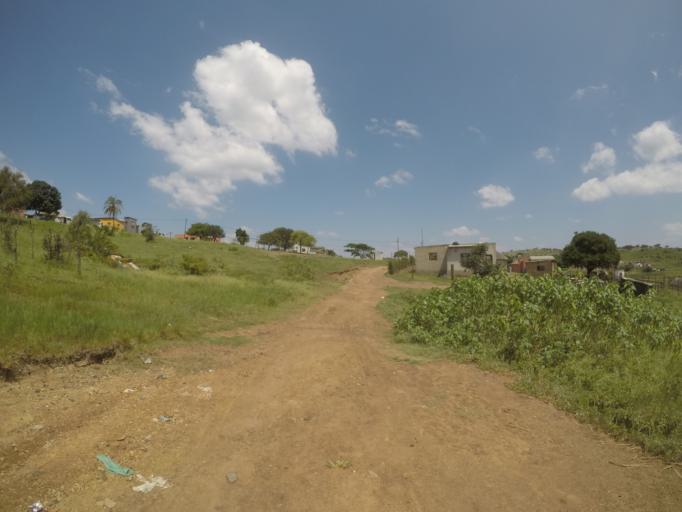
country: ZA
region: KwaZulu-Natal
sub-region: uThungulu District Municipality
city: Empangeni
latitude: -28.6020
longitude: 31.7405
